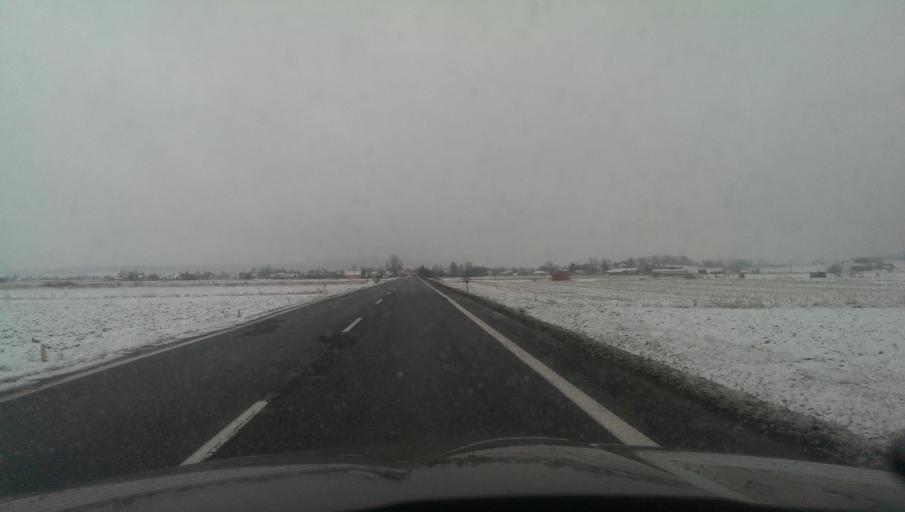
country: PL
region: Subcarpathian Voivodeship
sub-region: Powiat sanocki
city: Zarszyn
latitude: 49.5828
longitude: 21.9914
